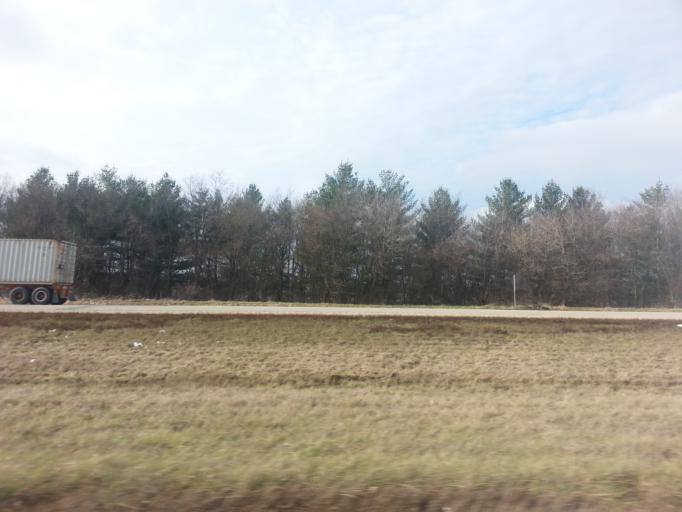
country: US
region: Illinois
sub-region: Winnebago County
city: Cherry Valley
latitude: 42.1921
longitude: -89.0238
